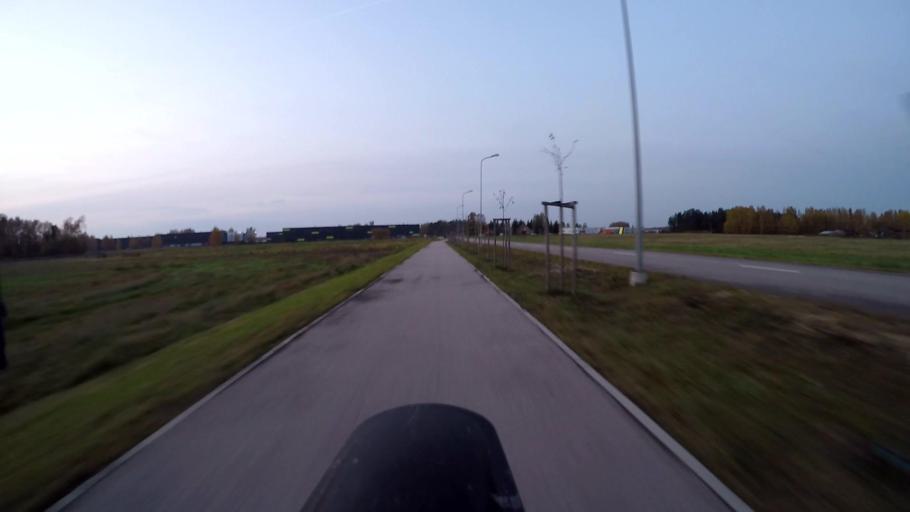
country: LV
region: Marupe
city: Marupe
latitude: 56.9144
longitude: 23.9940
